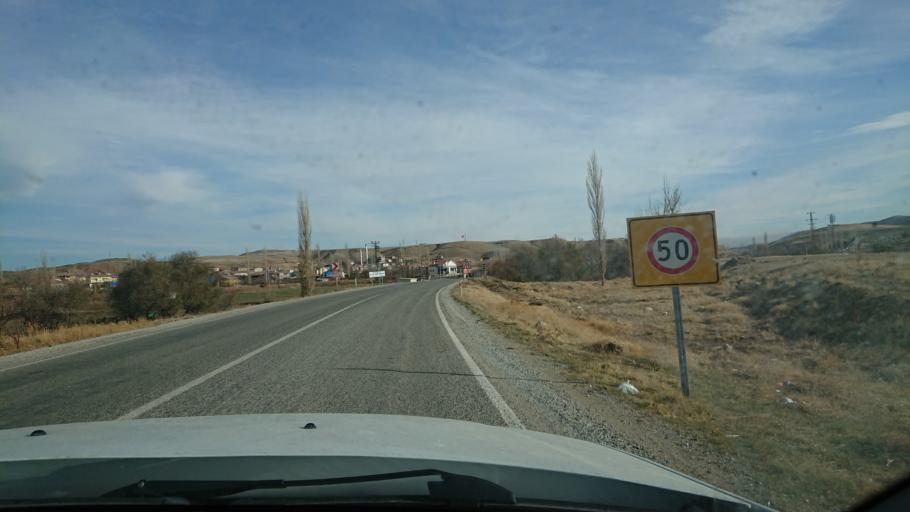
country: TR
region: Aksaray
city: Acipinar
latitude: 38.4810
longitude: 33.9026
